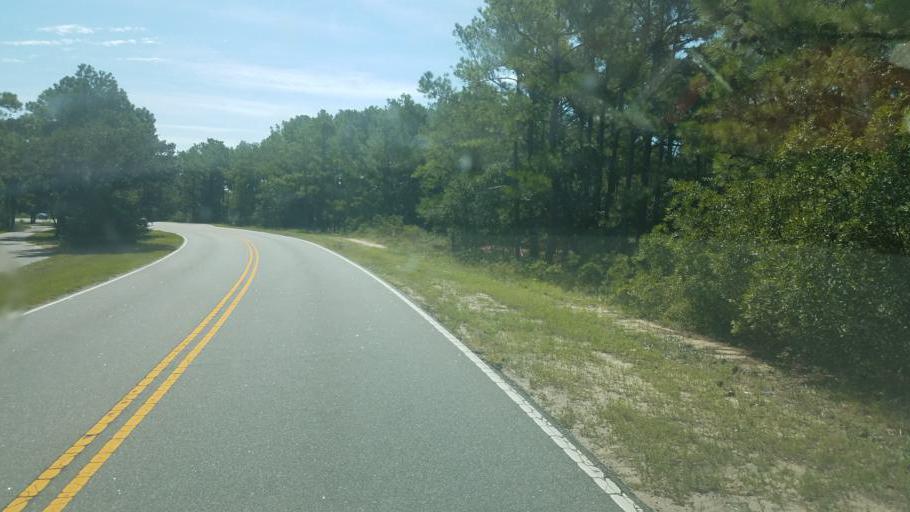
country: US
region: North Carolina
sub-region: Dare County
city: Kill Devil Hills
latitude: 36.0108
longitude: -75.6708
